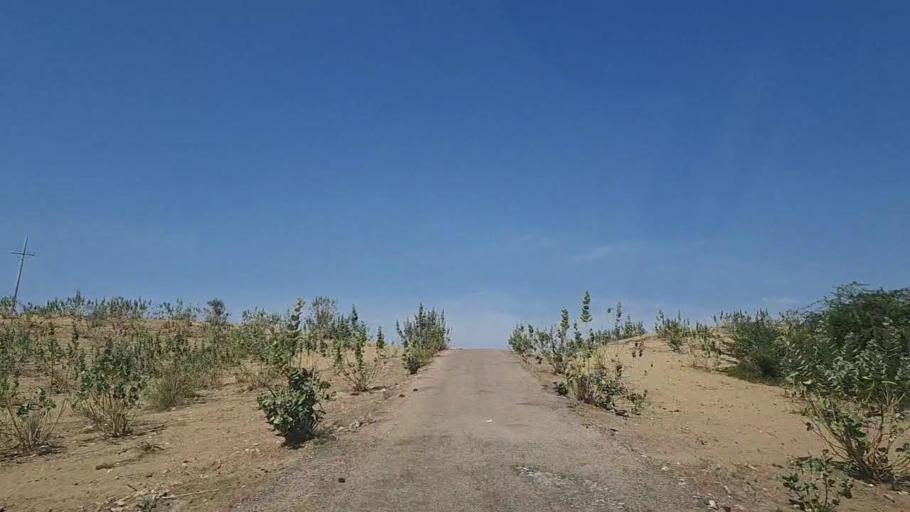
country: PK
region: Sindh
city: Mithi
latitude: 24.8585
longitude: 69.6694
